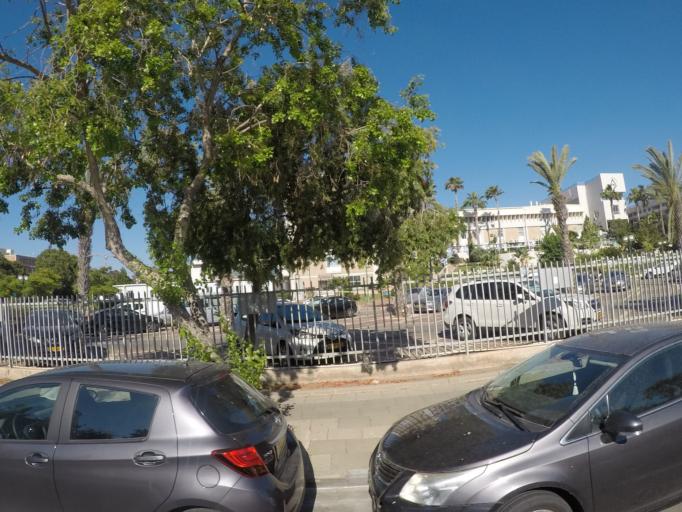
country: IL
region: Tel Aviv
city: Ramat Gan
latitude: 32.1100
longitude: 34.8017
